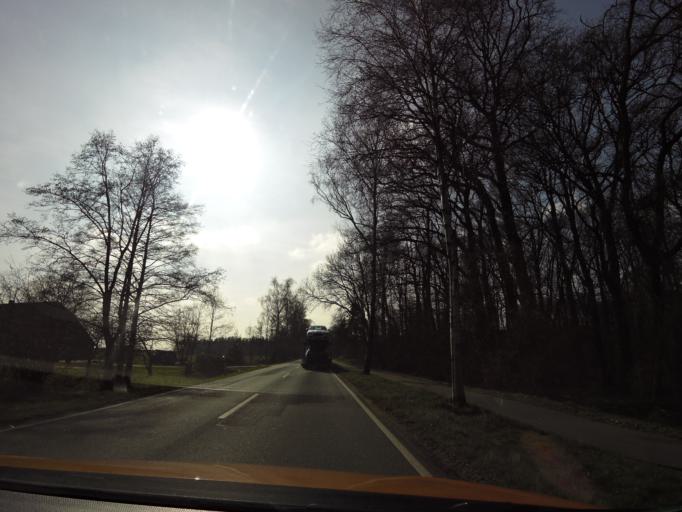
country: DE
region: Lower Saxony
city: Oldenburg
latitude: 53.1706
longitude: 8.3156
